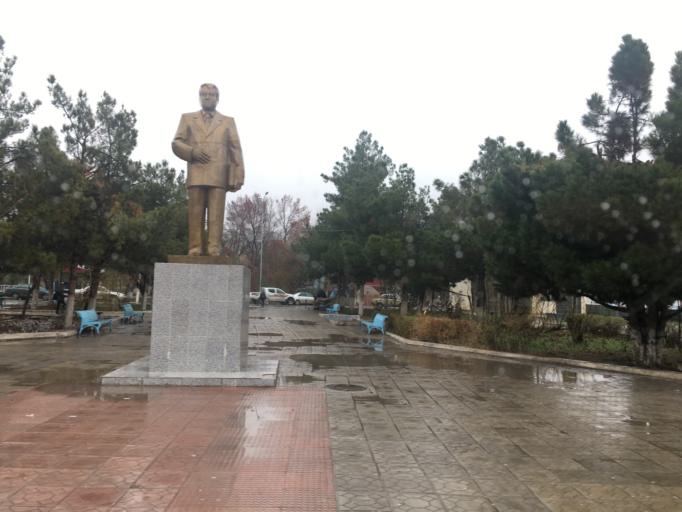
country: TM
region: Mary
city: Yoloeten
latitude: 37.2985
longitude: 62.3597
